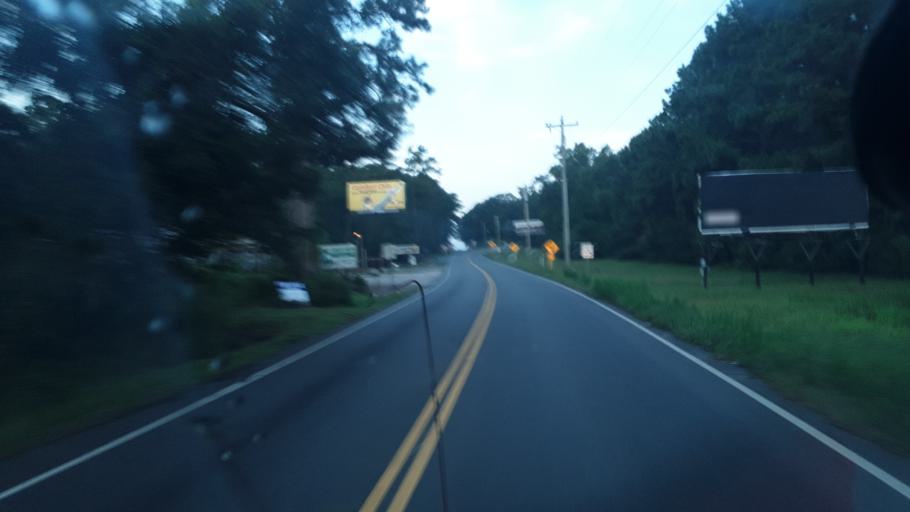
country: US
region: North Carolina
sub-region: Brunswick County
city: Carolina Shores
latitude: 33.8883
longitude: -78.5933
